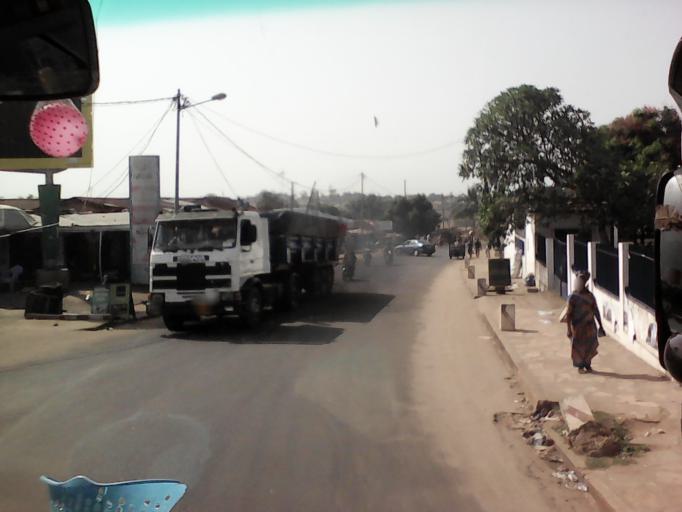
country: TG
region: Centrale
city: Sokode
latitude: 8.9825
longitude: 1.1409
